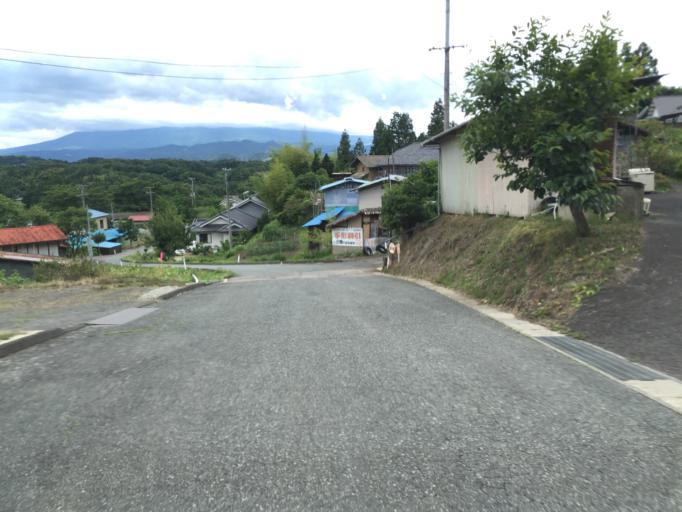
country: JP
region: Fukushima
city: Fukushima-shi
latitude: 37.6786
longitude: 140.5079
